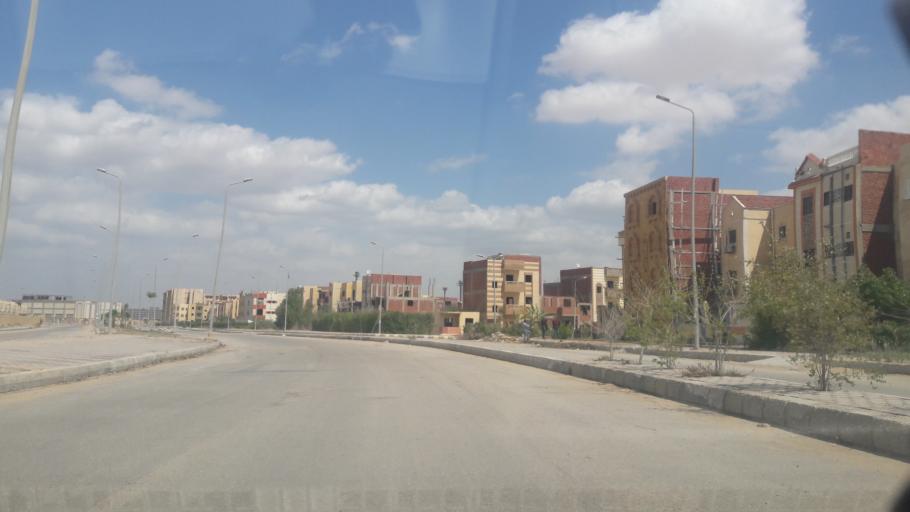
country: EG
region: Al Jizah
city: Madinat Sittah Uktubar
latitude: 29.9339
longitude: 31.0598
